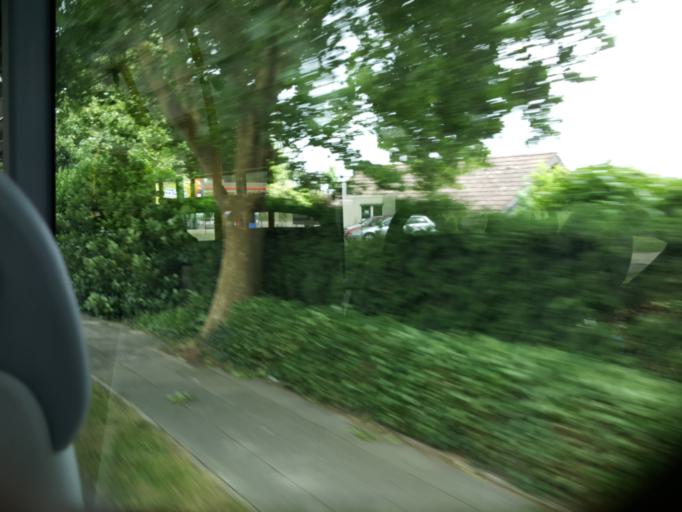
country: DE
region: North Rhine-Westphalia
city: Bad Oeynhausen
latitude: 52.2332
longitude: 8.8333
